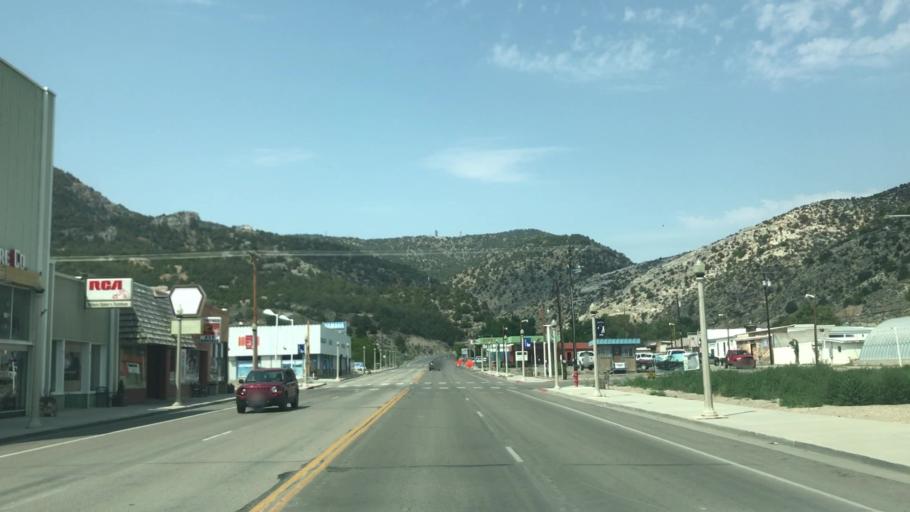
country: US
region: Nevada
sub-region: White Pine County
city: Ely
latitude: 39.2479
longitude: -114.8942
